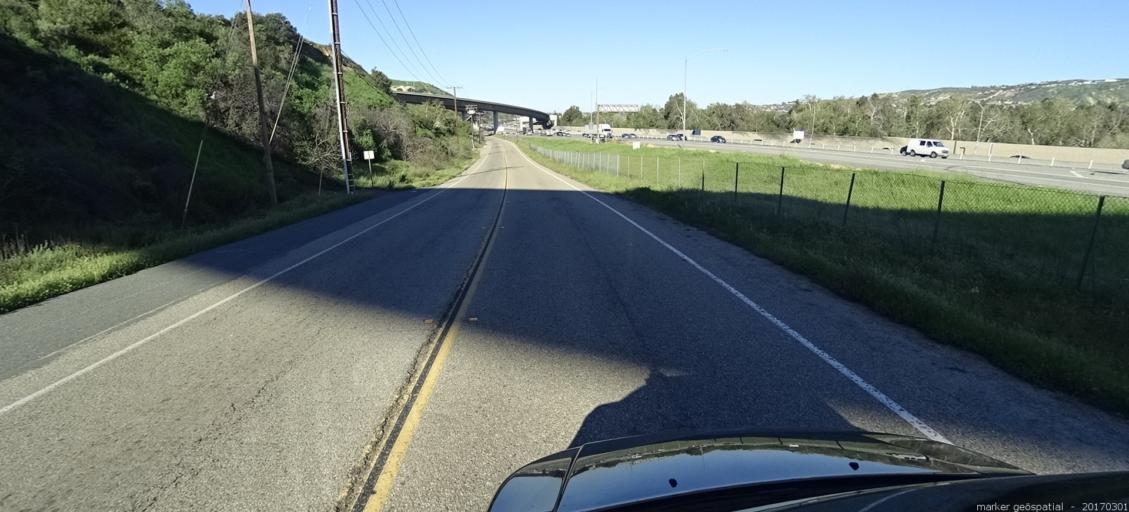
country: US
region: California
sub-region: Orange County
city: Yorba Linda
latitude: 33.8656
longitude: -117.7153
